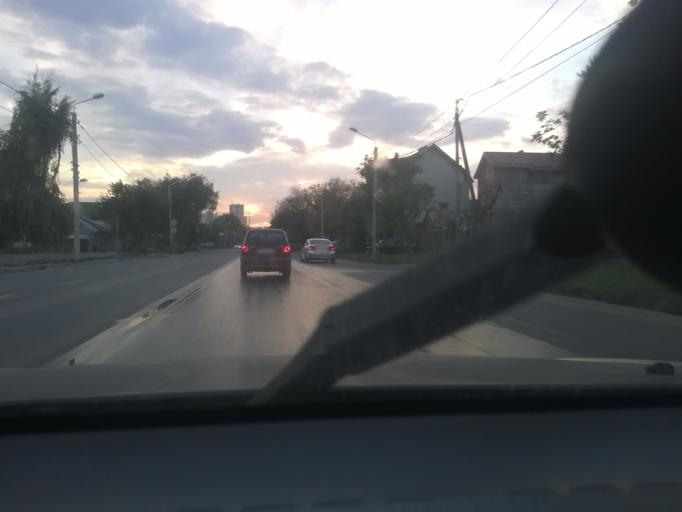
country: RU
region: Rostov
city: Rostov-na-Donu
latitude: 47.2294
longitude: 39.6793
